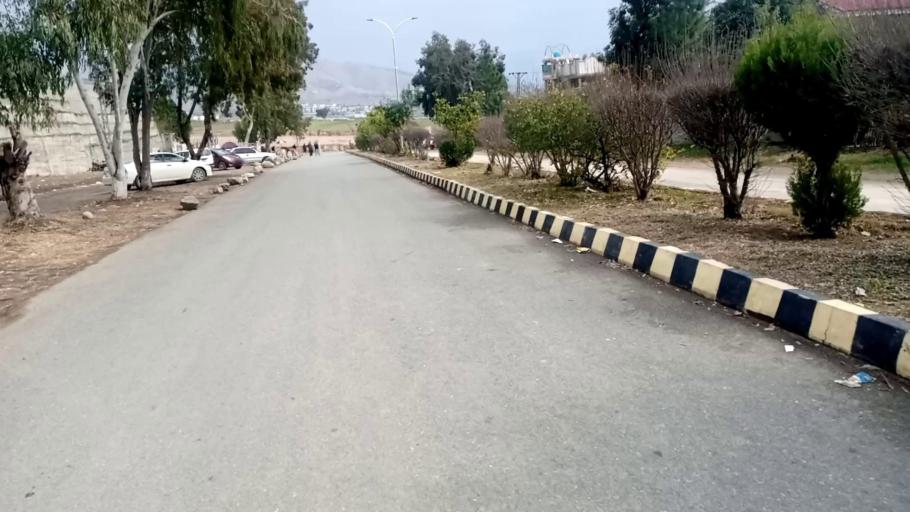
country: PK
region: Khyber Pakhtunkhwa
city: Mingora
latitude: 34.8315
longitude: 72.3534
